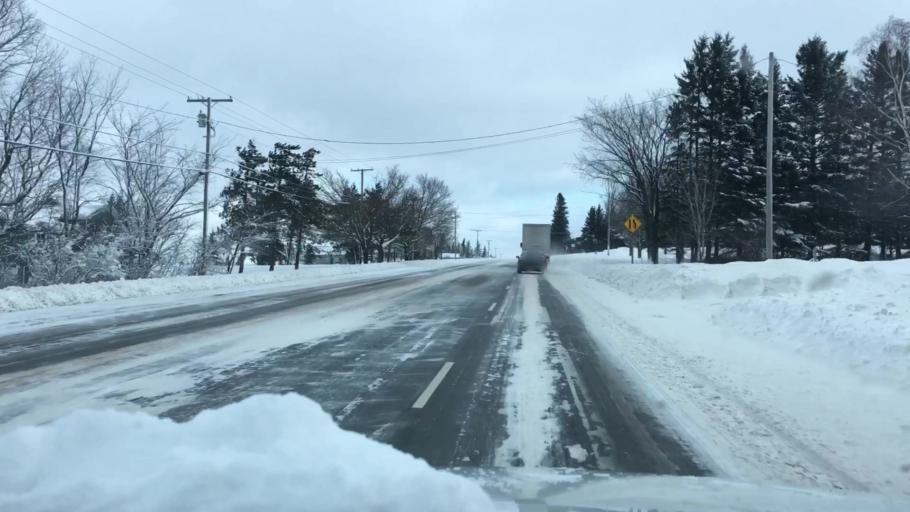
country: US
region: Maine
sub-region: Aroostook County
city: Presque Isle
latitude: 46.7261
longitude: -68.0040
